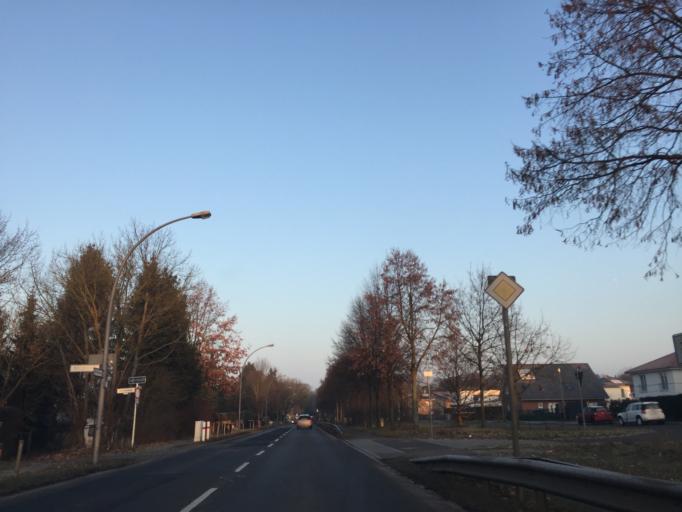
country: DE
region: Berlin
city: Kladow
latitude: 52.4729
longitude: 13.1222
